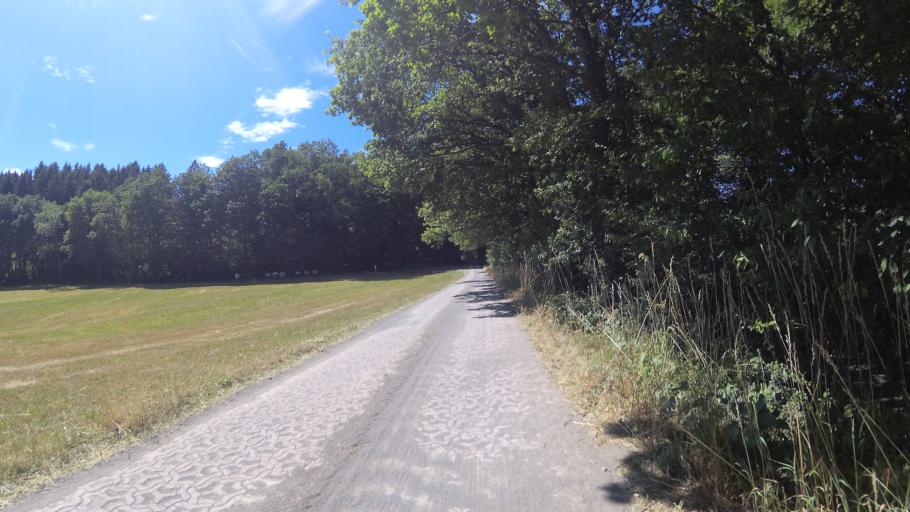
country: DE
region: Saarland
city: Namborn
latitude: 49.4920
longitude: 7.1344
